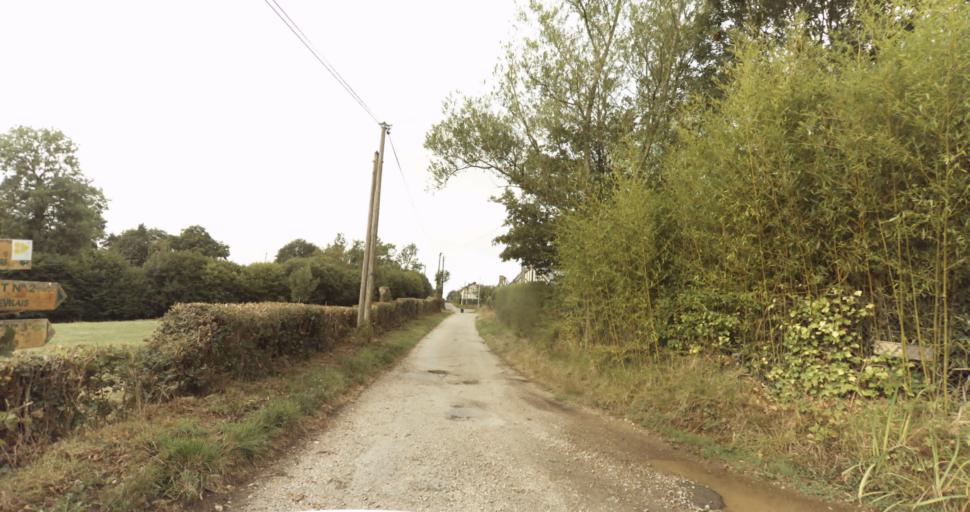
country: FR
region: Lower Normandy
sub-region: Departement de l'Orne
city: Vimoutiers
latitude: 48.9296
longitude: 0.1797
